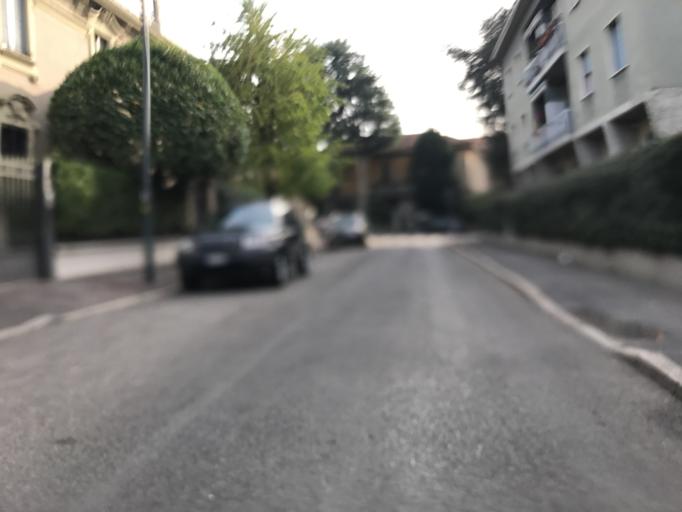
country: IT
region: Lombardy
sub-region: Citta metropolitana di Milano
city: Milano
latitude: 45.4994
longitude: 9.2015
